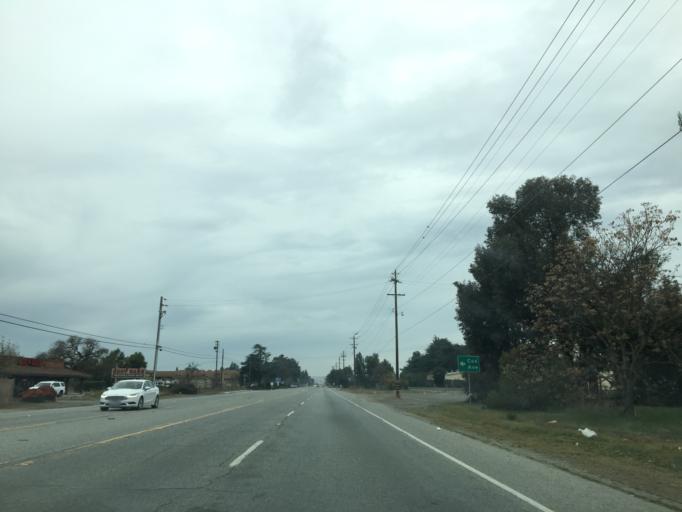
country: US
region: California
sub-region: Santa Clara County
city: San Martin
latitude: 37.0783
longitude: -121.6064
